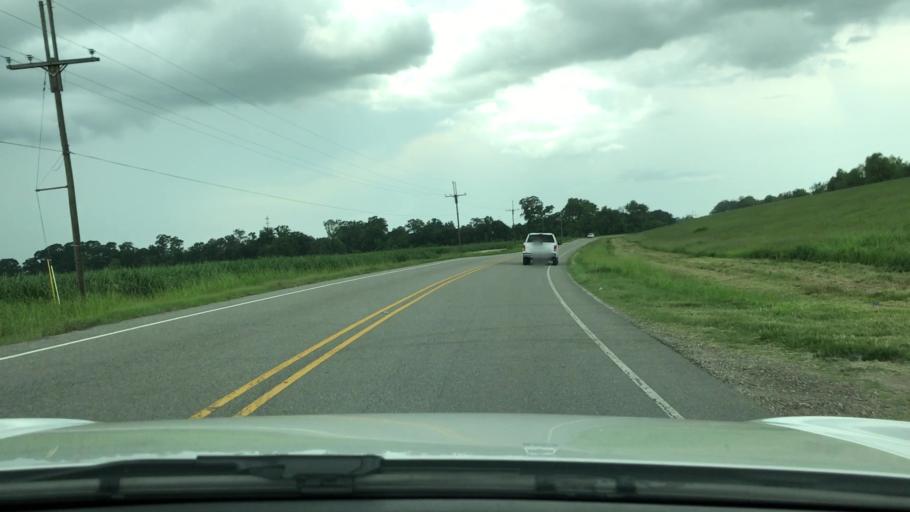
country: US
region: Louisiana
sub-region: Iberville Parish
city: Plaquemine
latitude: 30.2733
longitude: -91.2041
